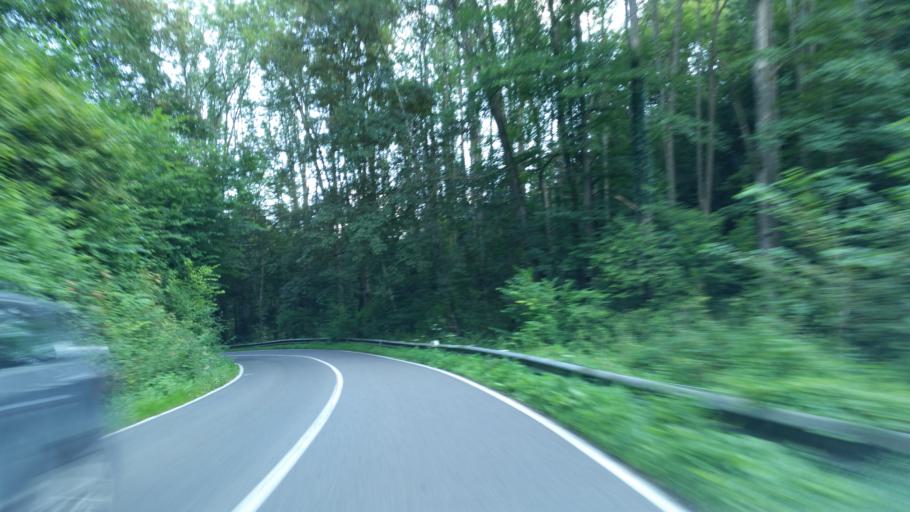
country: BE
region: Wallonia
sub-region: Province du Luxembourg
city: Durbuy
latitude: 50.3622
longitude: 5.4541
